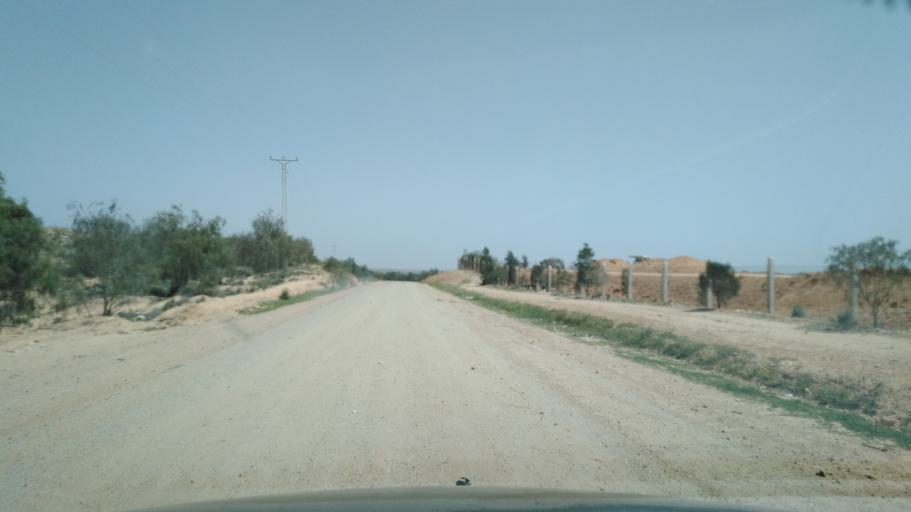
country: TN
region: Safaqis
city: Sfax
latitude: 34.7104
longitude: 10.5257
